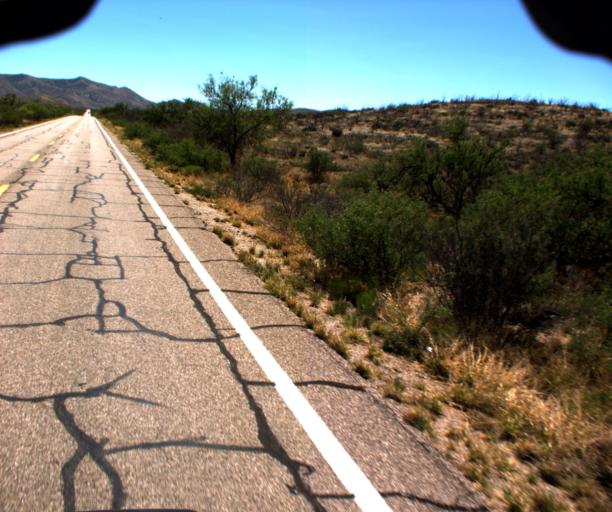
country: US
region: Arizona
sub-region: Pima County
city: Vail
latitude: 31.9500
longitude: -110.6666
